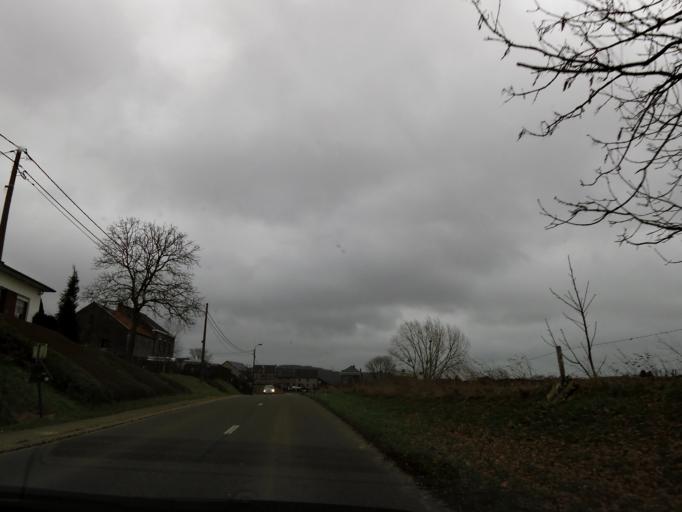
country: BE
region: Wallonia
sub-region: Province de Liege
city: Plombieres
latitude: 50.7474
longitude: 5.9875
